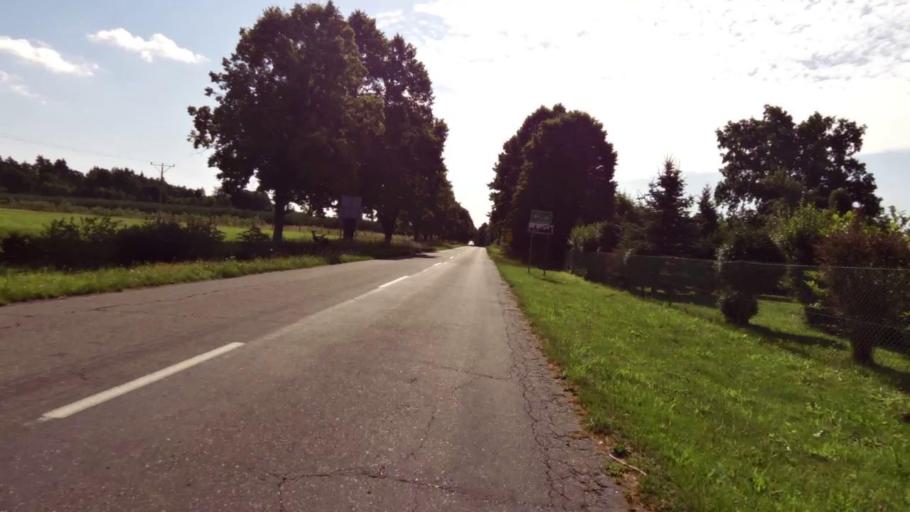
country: PL
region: West Pomeranian Voivodeship
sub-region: Powiat stargardzki
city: Dobrzany
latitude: 53.3712
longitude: 15.3723
